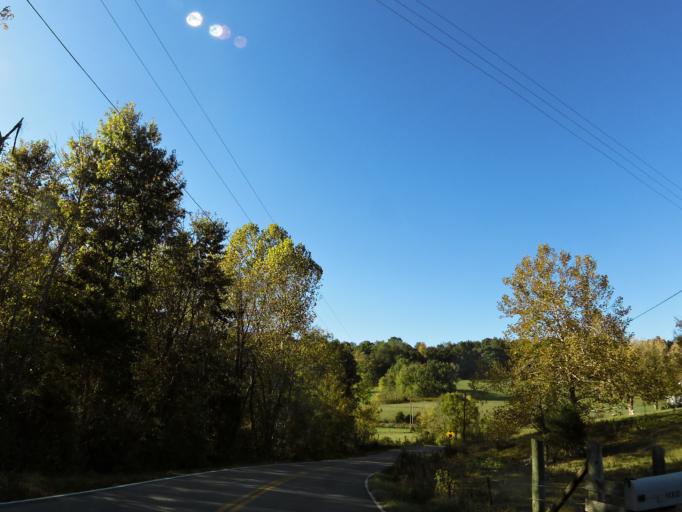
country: US
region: Tennessee
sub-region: Union County
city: Luttrell
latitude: 36.2594
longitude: -83.6545
